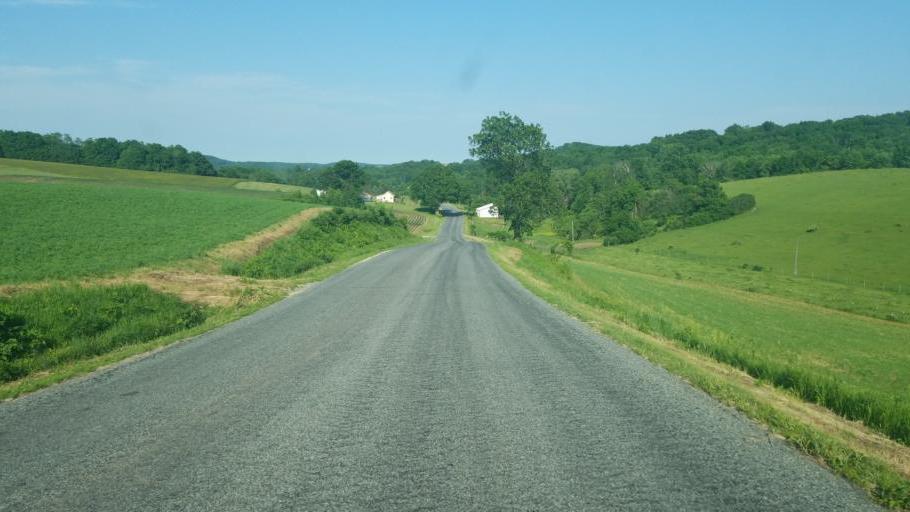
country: US
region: Wisconsin
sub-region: Vernon County
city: Hillsboro
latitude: 43.6813
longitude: -90.3669
